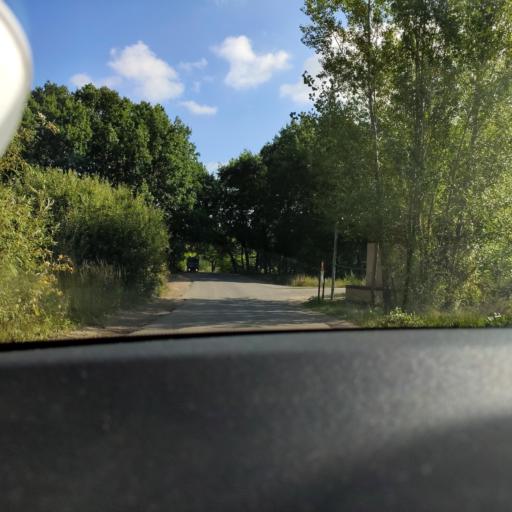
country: RU
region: Samara
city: Volzhskiy
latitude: 53.4326
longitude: 50.0870
